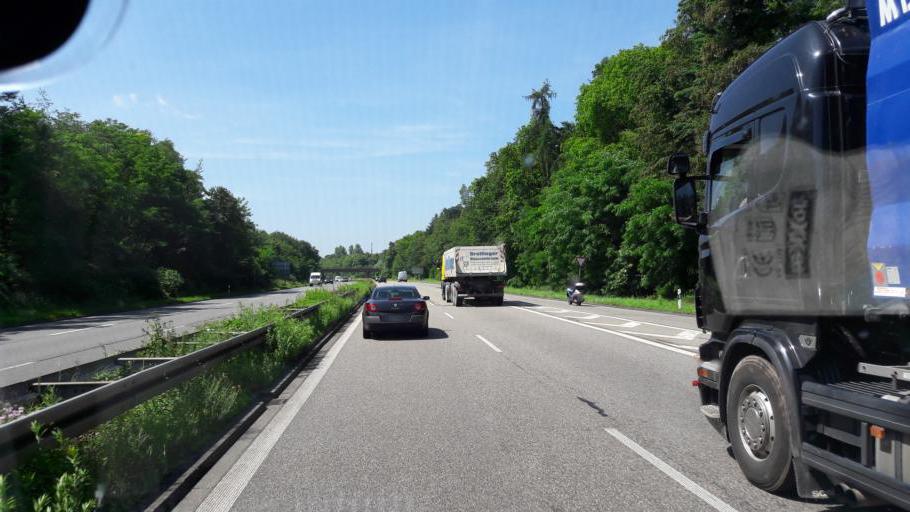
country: DE
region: Baden-Wuerttemberg
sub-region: Karlsruhe Region
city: Ettlingen
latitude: 48.9584
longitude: 8.3784
